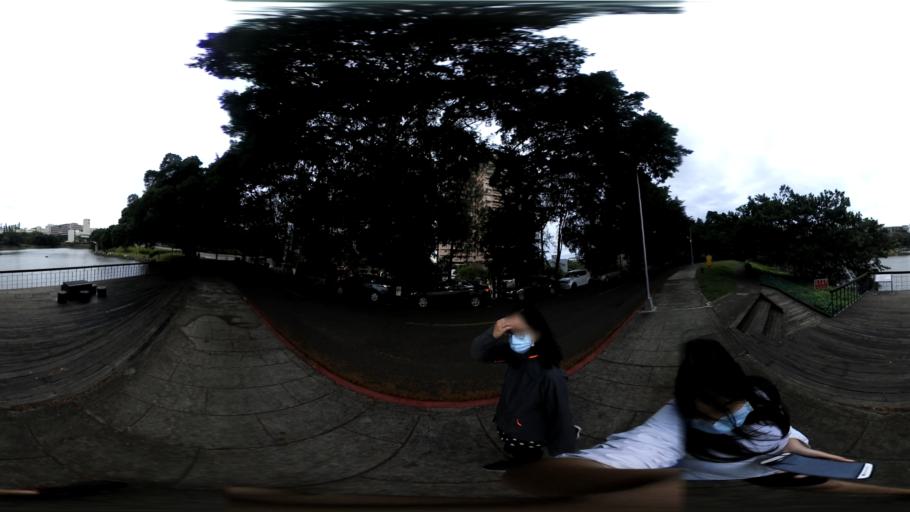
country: TW
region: Taiwan
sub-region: Hsinchu
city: Hsinchu
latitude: 24.7891
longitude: 121.0006
